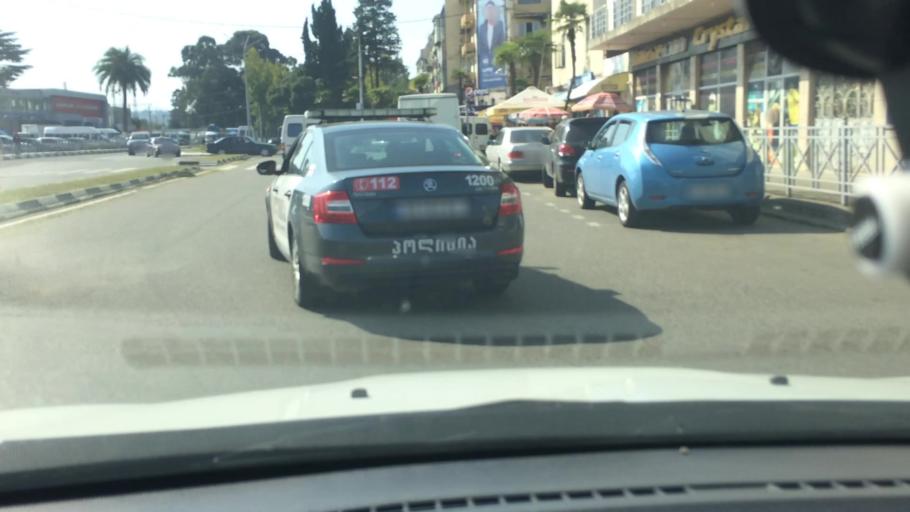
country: GE
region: Ajaria
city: Kobuleti
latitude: 41.8111
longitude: 41.7803
